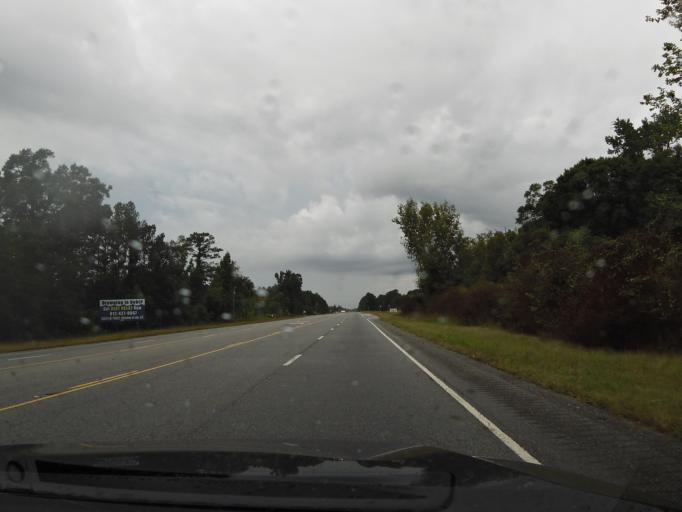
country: US
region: Georgia
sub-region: Wayne County
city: Jesup
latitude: 31.5362
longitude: -81.7961
